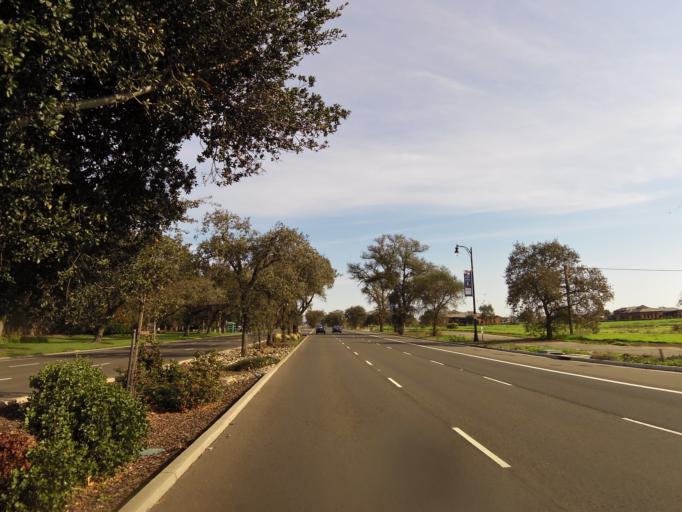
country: US
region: California
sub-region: Sacramento County
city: Laguna
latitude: 38.4090
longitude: -121.4032
